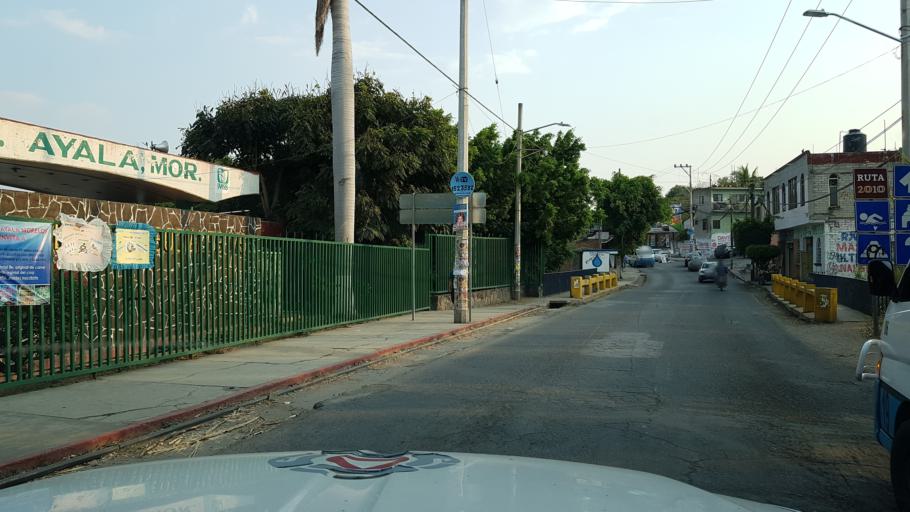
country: MX
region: Morelos
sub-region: Ayala
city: Ciudad Ayala
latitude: 18.7706
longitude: -98.9832
